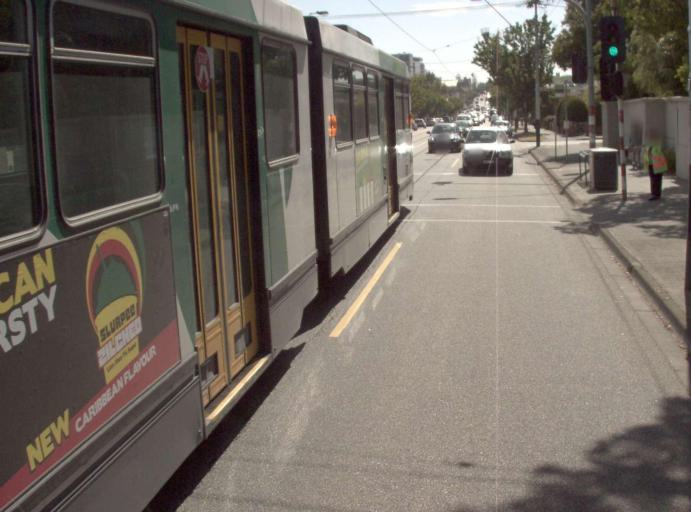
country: AU
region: Victoria
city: Glen Huntly
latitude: -37.8768
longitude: 145.0551
